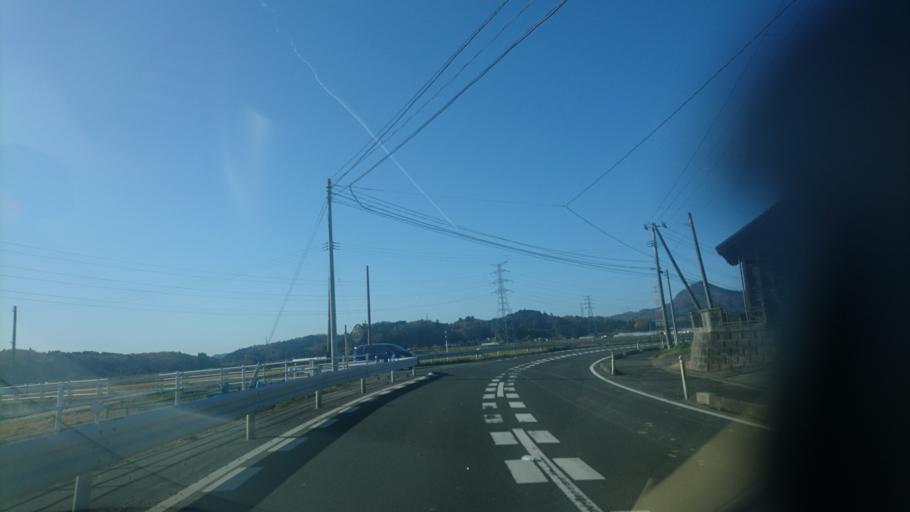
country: JP
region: Miyagi
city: Tomiya
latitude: 38.4143
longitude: 140.8798
